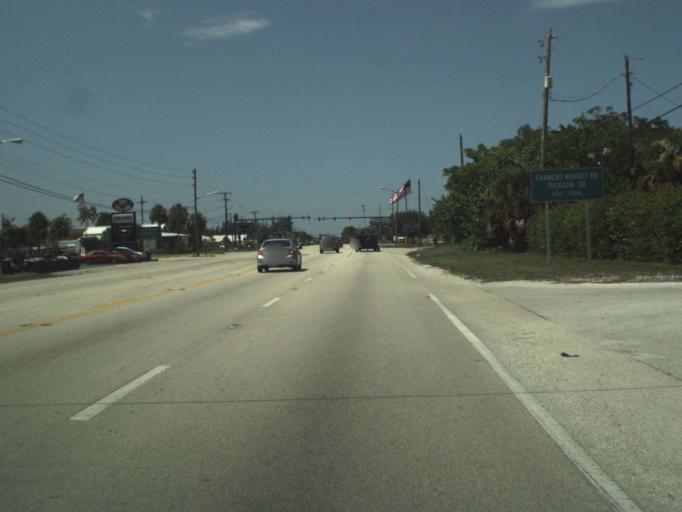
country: US
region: Florida
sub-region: Saint Lucie County
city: White City
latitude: 27.3952
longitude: -80.3255
